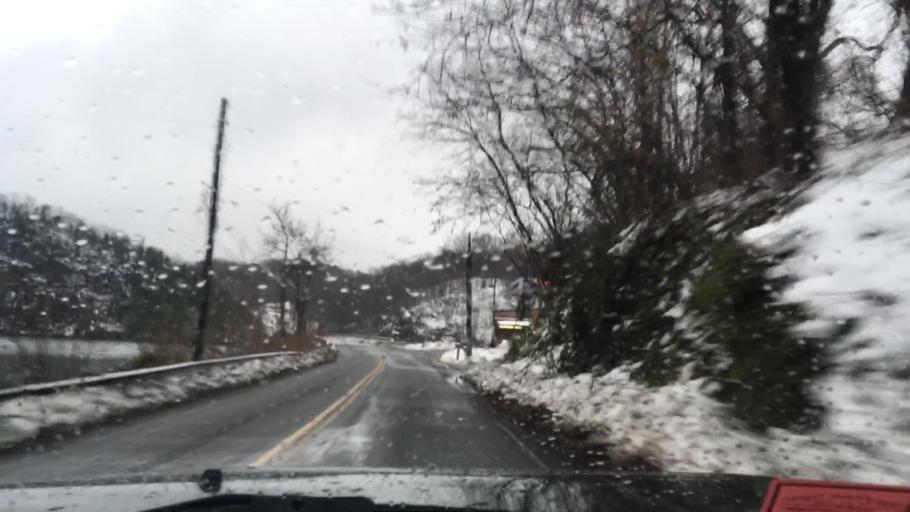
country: US
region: Virginia
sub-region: Pulaski County
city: Dublin
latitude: 37.0045
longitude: -80.6850
